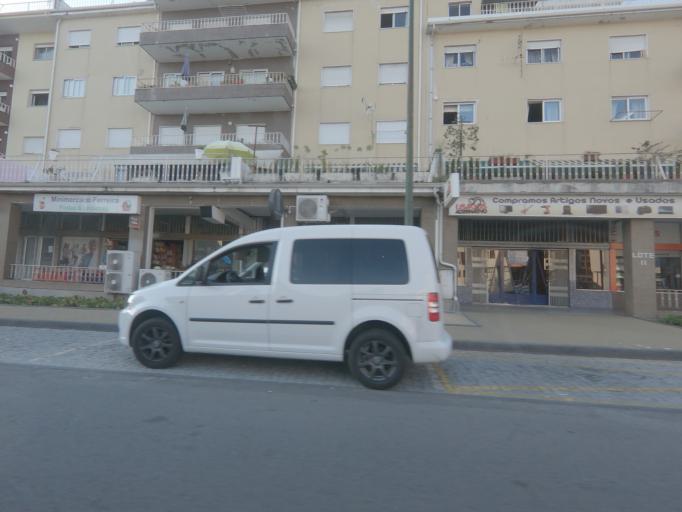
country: PT
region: Vila Real
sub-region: Vila Real
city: Vila Real
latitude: 41.3065
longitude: -7.7432
